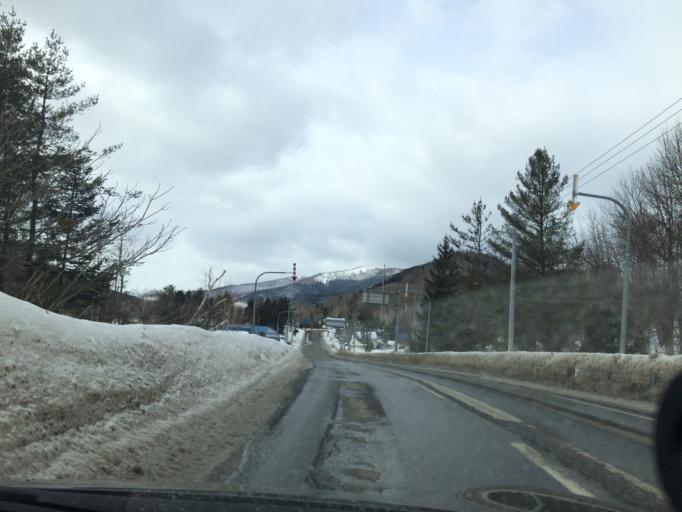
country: JP
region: Hokkaido
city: Shimo-furano
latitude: 43.1225
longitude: 142.6798
